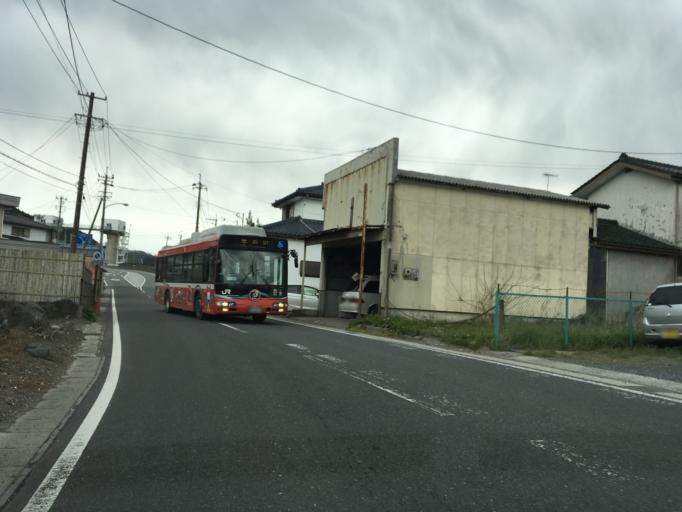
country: JP
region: Miyagi
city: Wakuya
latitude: 38.6053
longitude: 141.3005
